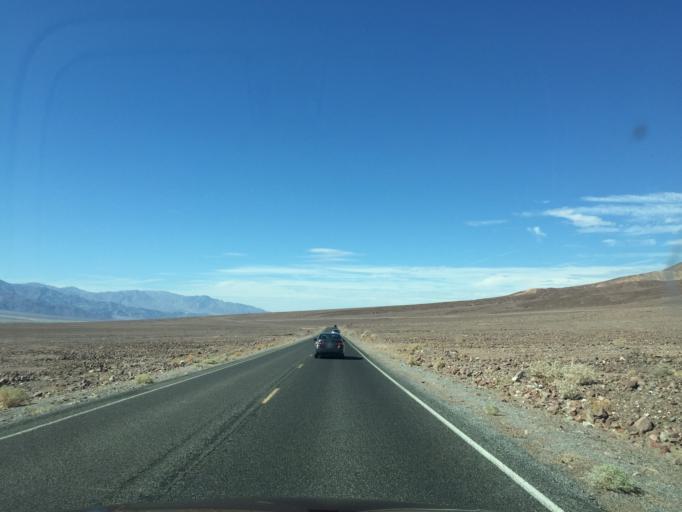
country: US
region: Nevada
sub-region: Nye County
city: Beatty
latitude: 36.2647
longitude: -116.7827
